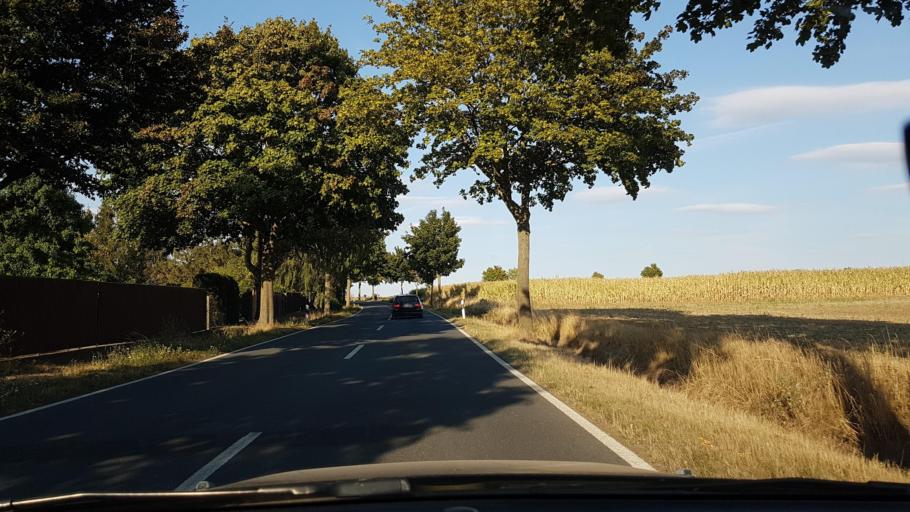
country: DE
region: Lower Saxony
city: Wunstorf
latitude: 52.4559
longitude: 9.4040
